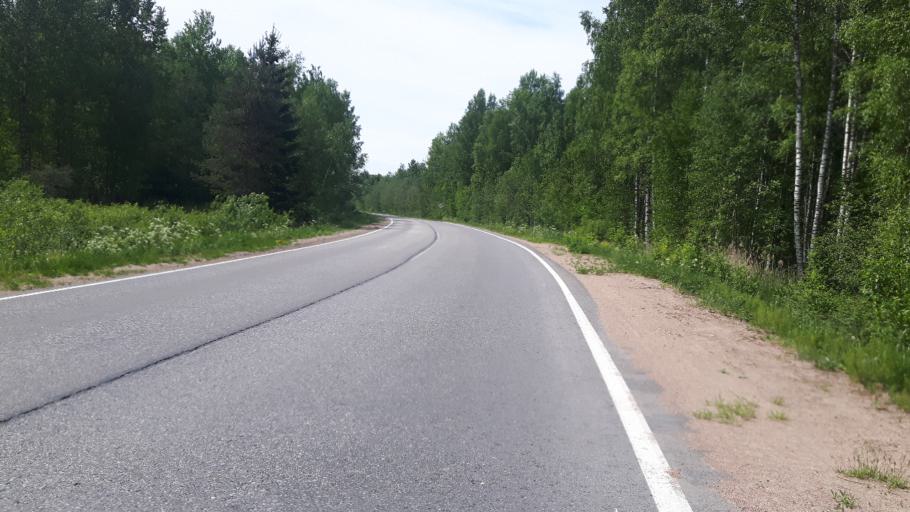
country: RU
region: Leningrad
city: Ust'-Luga
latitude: 59.6468
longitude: 28.2023
